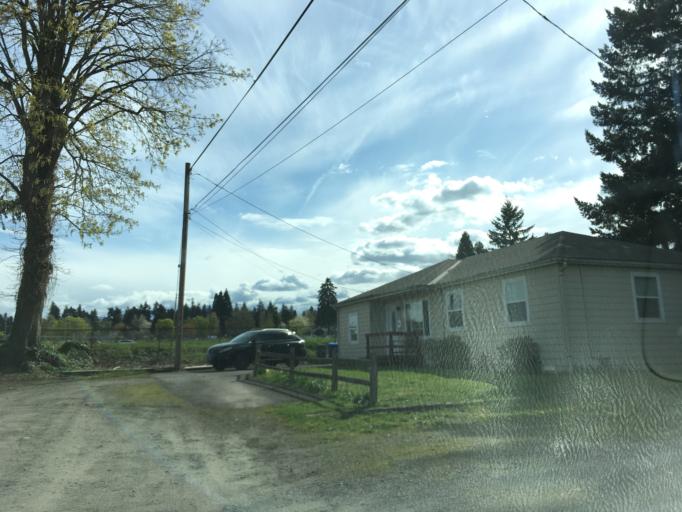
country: US
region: Oregon
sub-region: Multnomah County
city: Lents
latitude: 45.5548
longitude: -122.5433
